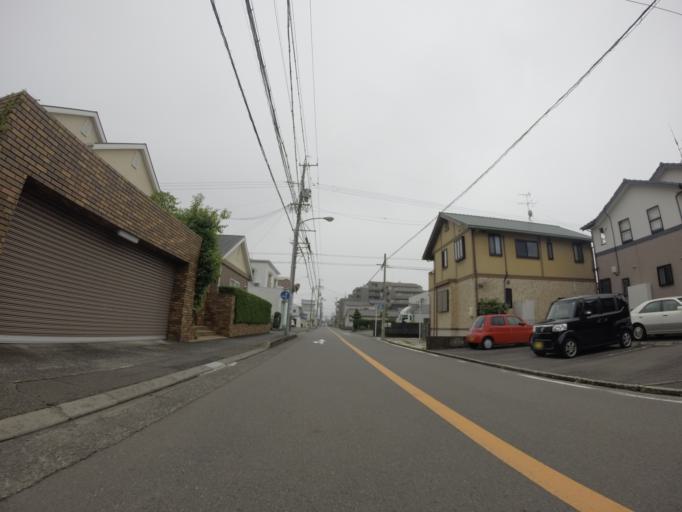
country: JP
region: Shizuoka
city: Shizuoka-shi
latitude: 34.9587
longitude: 138.3977
